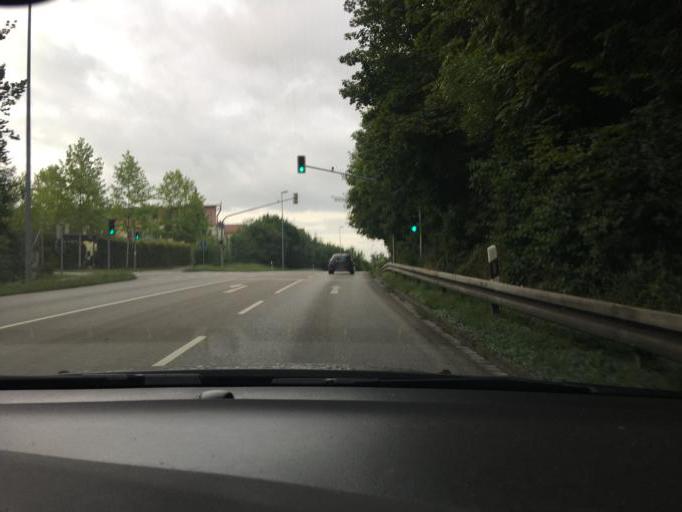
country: DE
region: Bavaria
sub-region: Upper Bavaria
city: Erding
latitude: 48.3073
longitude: 11.9189
